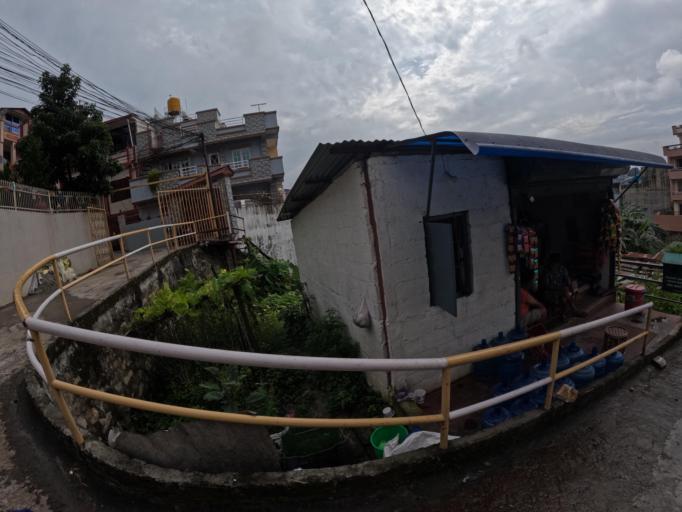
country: NP
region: Central Region
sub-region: Bagmati Zone
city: Kathmandu
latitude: 27.7518
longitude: 85.3217
